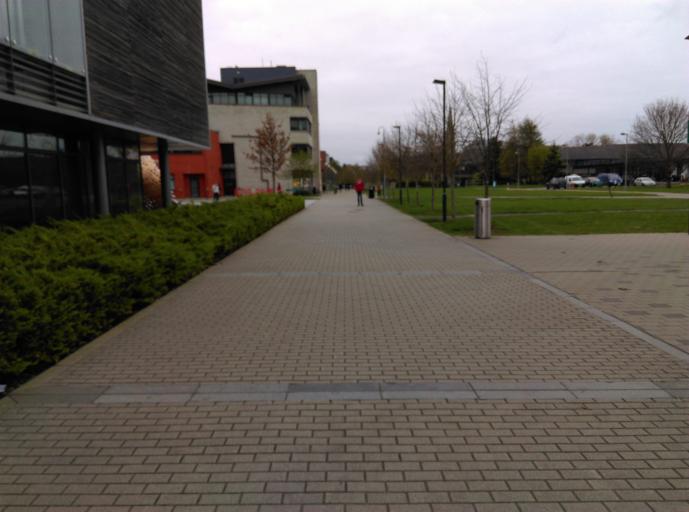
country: IE
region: Leinster
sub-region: Kildare
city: Maynooth
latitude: 53.3847
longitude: -6.6011
